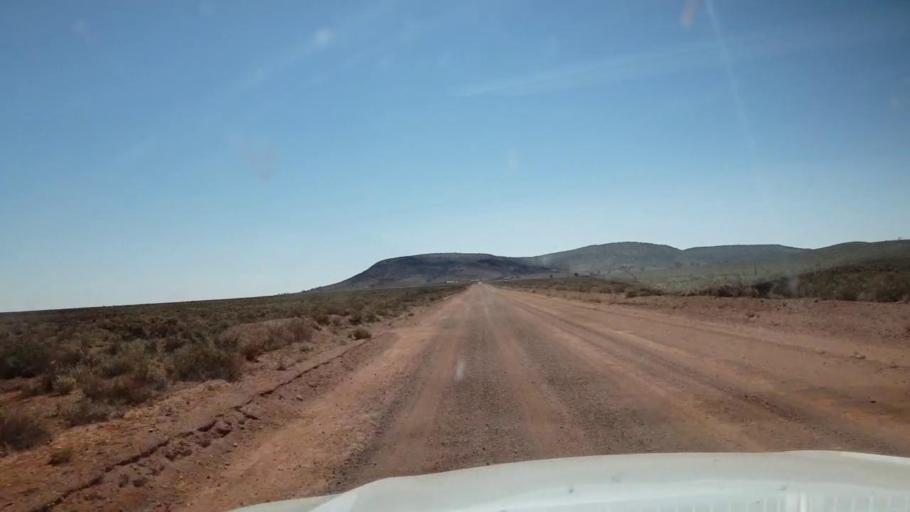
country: AU
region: South Australia
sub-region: Whyalla
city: Whyalla
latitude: -32.7037
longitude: 137.1361
